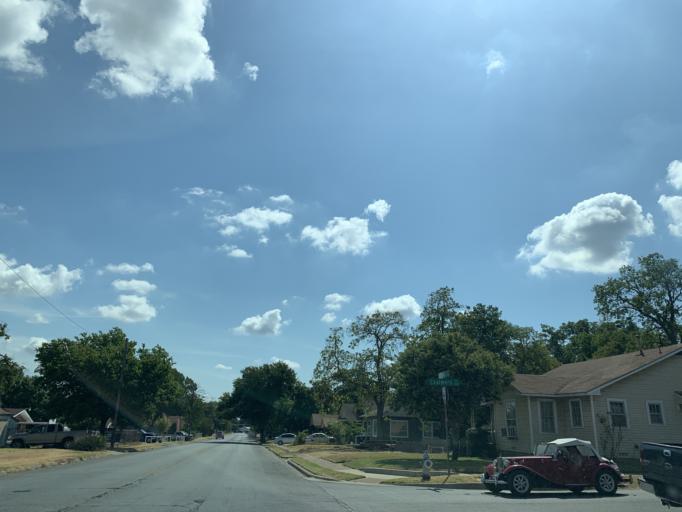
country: US
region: Texas
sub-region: Dallas County
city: Cockrell Hill
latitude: 32.7349
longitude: -96.8616
